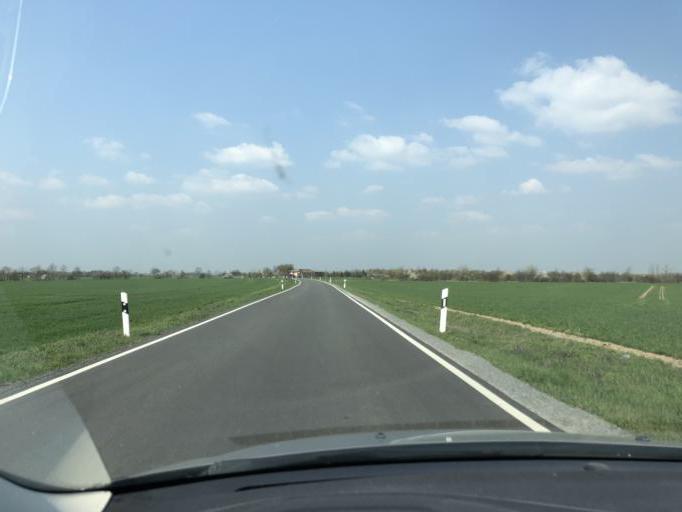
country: DE
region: Saxony
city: Wiedemar
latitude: 51.4854
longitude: 12.2213
